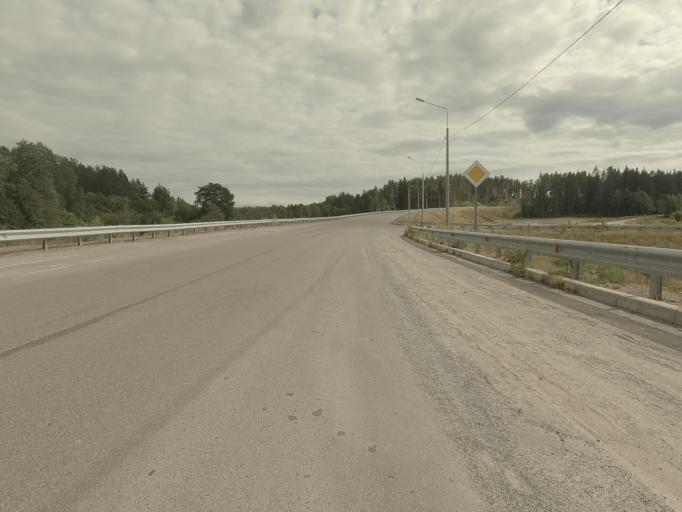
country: RU
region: Leningrad
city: Kamennogorsk
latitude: 60.9649
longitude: 29.1409
